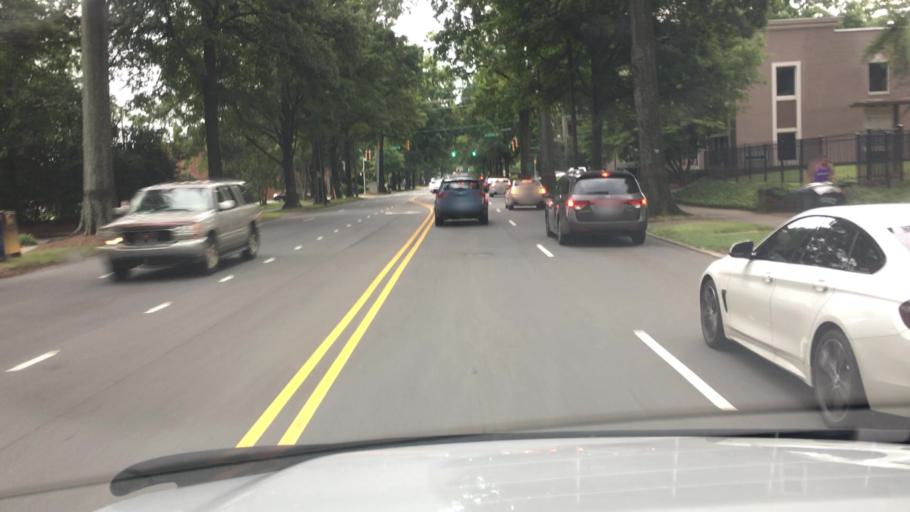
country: US
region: North Carolina
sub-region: Mecklenburg County
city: Charlotte
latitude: 35.2168
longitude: -80.8474
